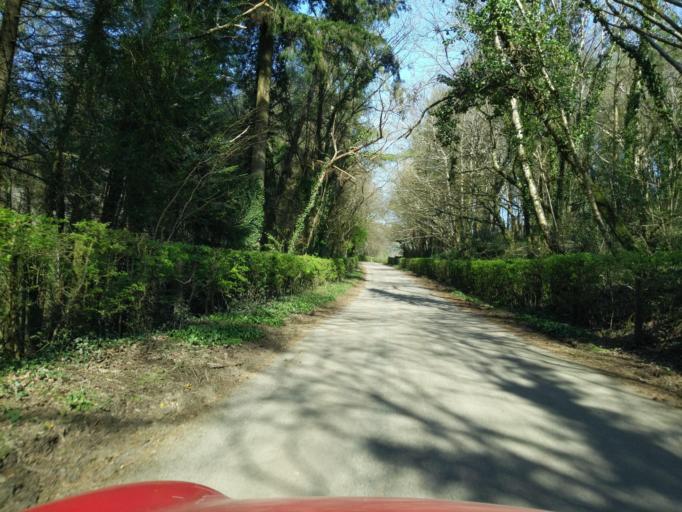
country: GB
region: England
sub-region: Devon
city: Bere Alston
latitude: 50.4626
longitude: -4.1385
